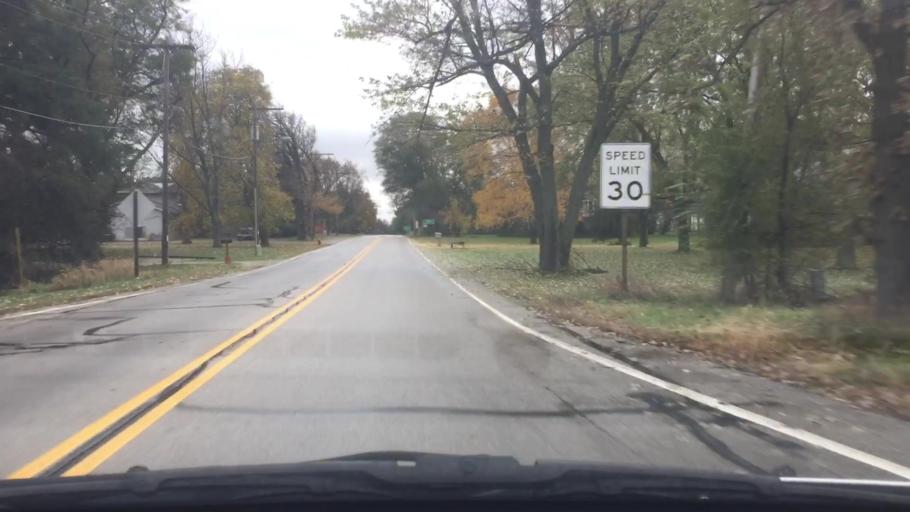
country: US
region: Wisconsin
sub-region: Waukesha County
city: Eagle
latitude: 42.8850
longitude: -88.4737
